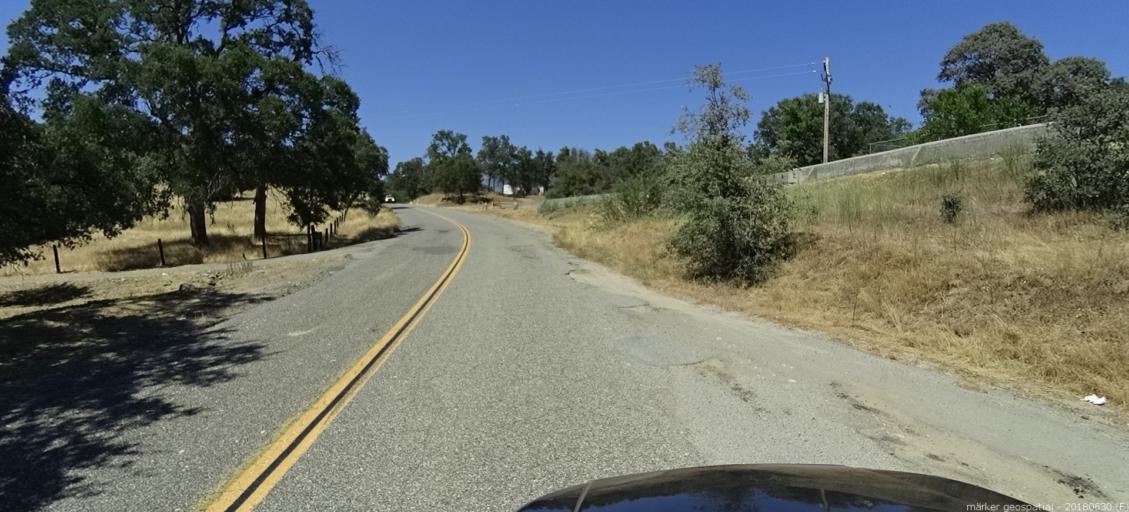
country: US
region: California
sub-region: Fresno County
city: Auberry
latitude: 37.1887
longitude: -119.5039
